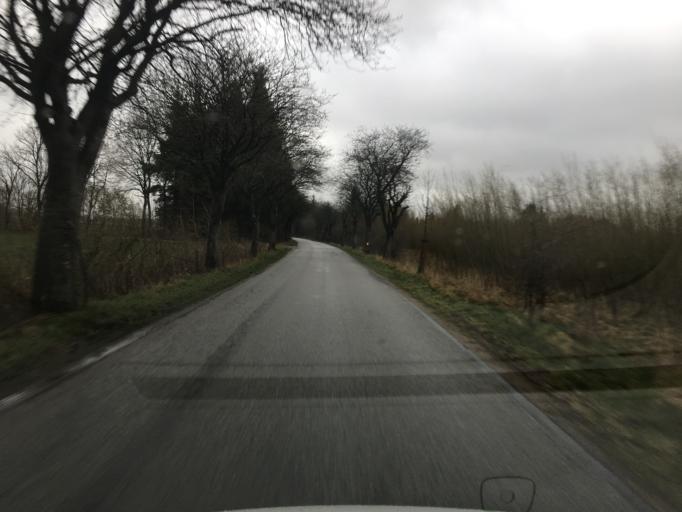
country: DK
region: South Denmark
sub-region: Aabenraa Kommune
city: Padborg
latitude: 54.8996
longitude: 9.3429
